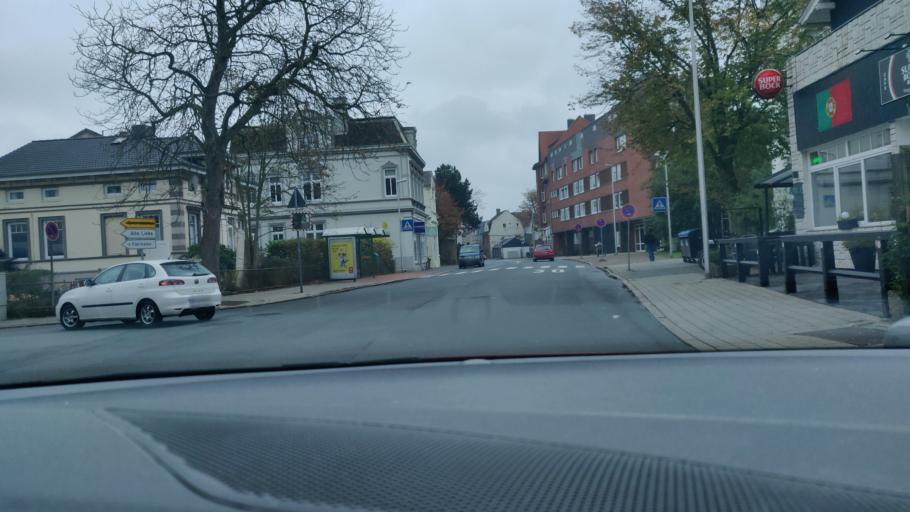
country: DE
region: Lower Saxony
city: Cuxhaven
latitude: 53.8721
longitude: 8.6976
